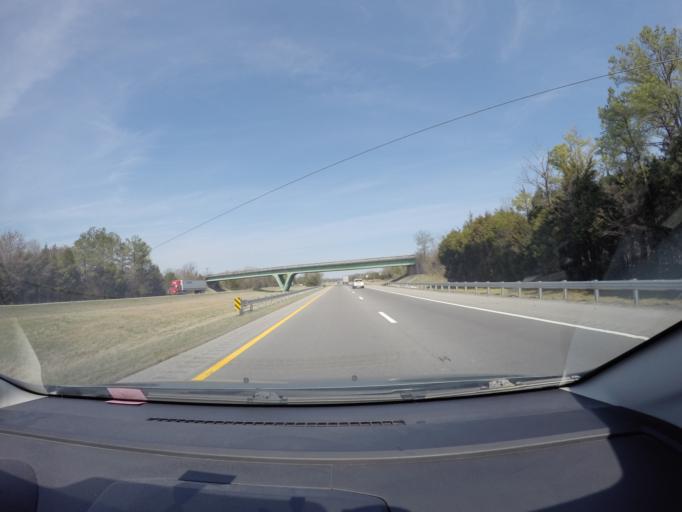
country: US
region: Tennessee
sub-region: Rutherford County
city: Plainview
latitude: 35.7632
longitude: -86.3546
